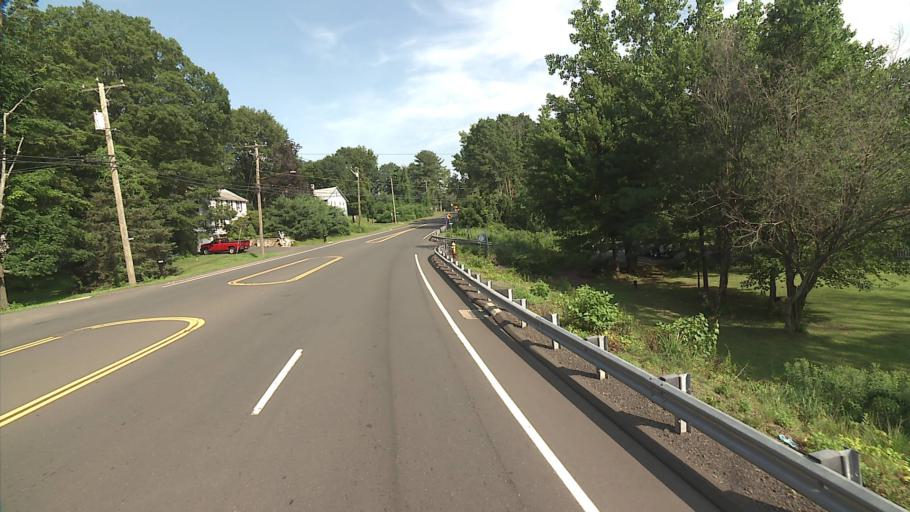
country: US
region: Connecticut
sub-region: New Haven County
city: Prospect
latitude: 41.5431
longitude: -72.9560
